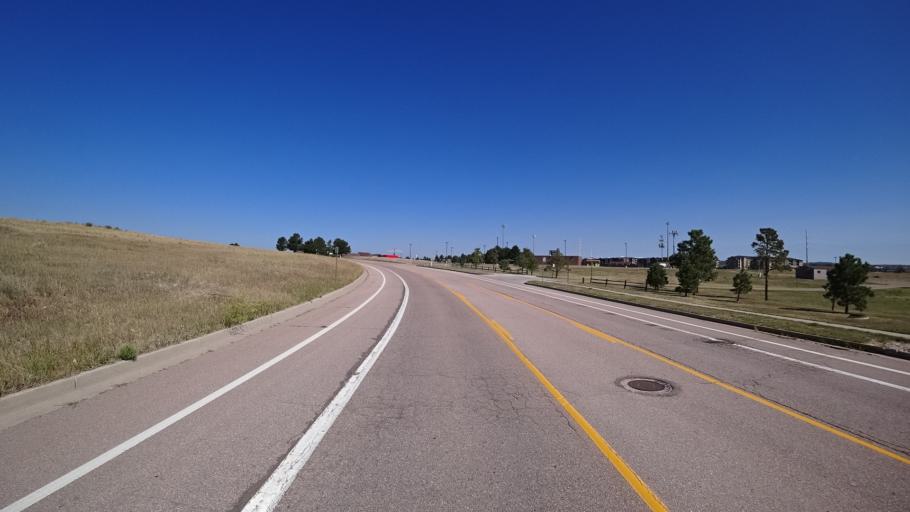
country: US
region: Colorado
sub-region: El Paso County
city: Black Forest
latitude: 38.9567
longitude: -104.7330
